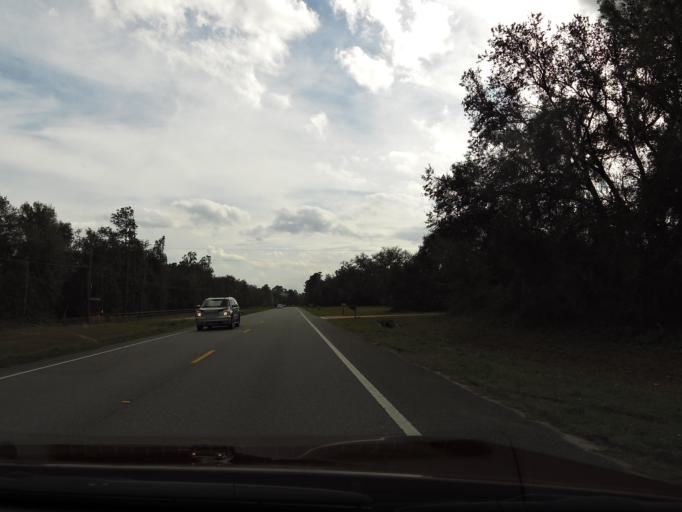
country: US
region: Florida
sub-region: Volusia County
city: De Leon Springs
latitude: 29.2123
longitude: -81.3152
